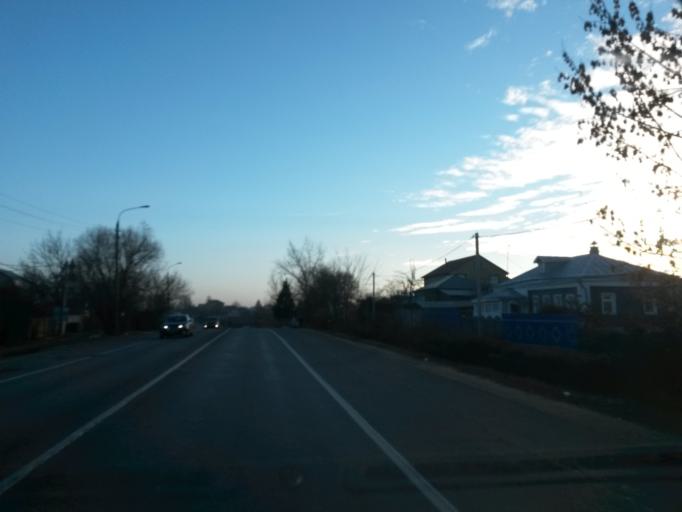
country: RU
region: Moskovskaya
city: Stolbovaya
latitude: 55.2777
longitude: 37.5099
